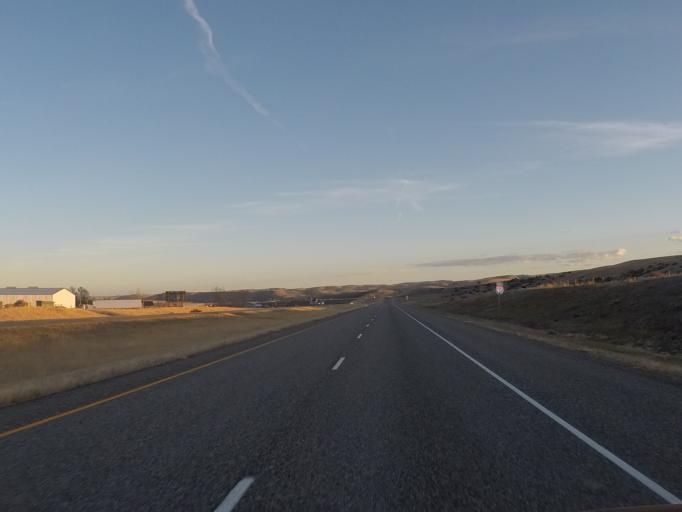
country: US
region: Montana
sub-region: Sweet Grass County
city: Big Timber
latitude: 45.7638
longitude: -109.7892
